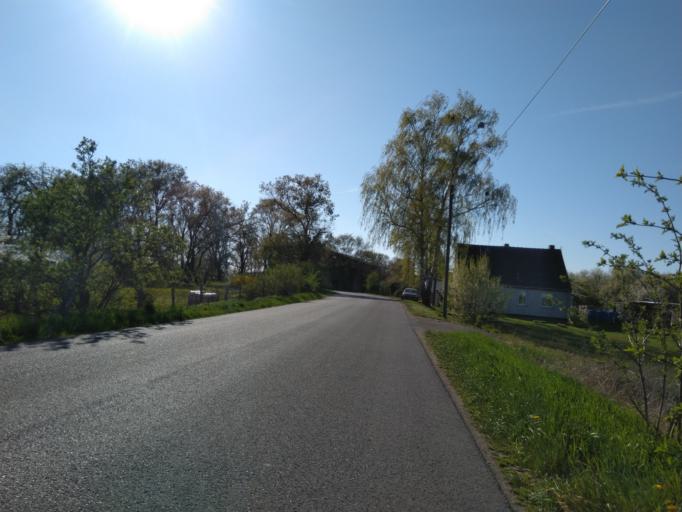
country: DE
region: Brandenburg
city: Bliesdorf
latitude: 52.7105
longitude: 14.1894
